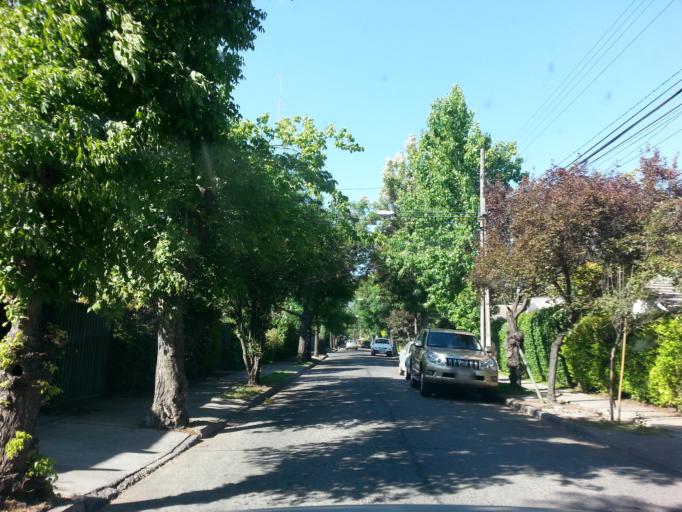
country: CL
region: Santiago Metropolitan
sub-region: Provincia de Santiago
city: Villa Presidente Frei, Nunoa, Santiago, Chile
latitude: -33.3919
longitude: -70.5867
